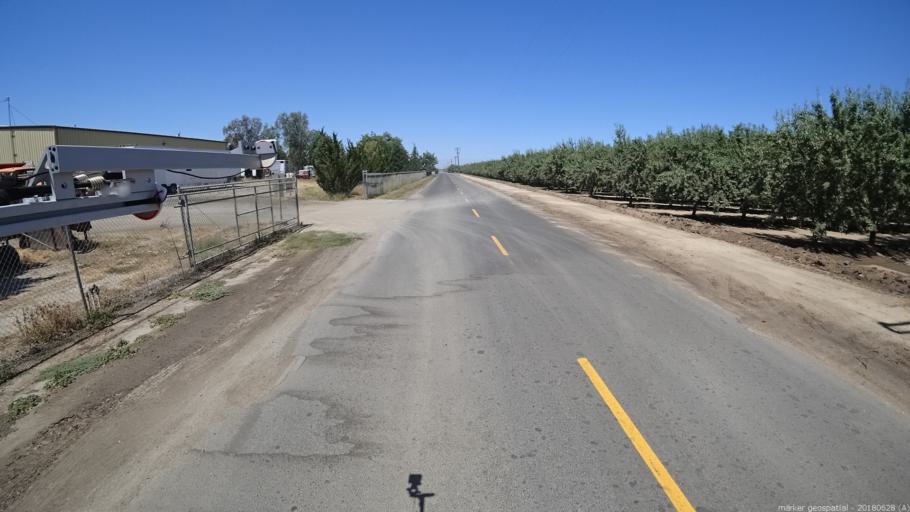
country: US
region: California
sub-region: Madera County
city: Parksdale
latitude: 36.9319
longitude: -120.0166
